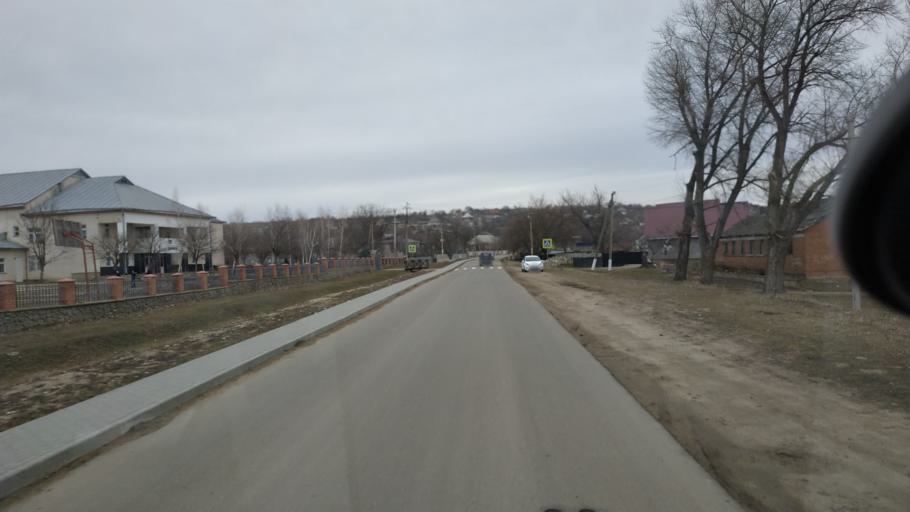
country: MD
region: Telenesti
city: Cocieri
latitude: 47.2689
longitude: 29.0568
